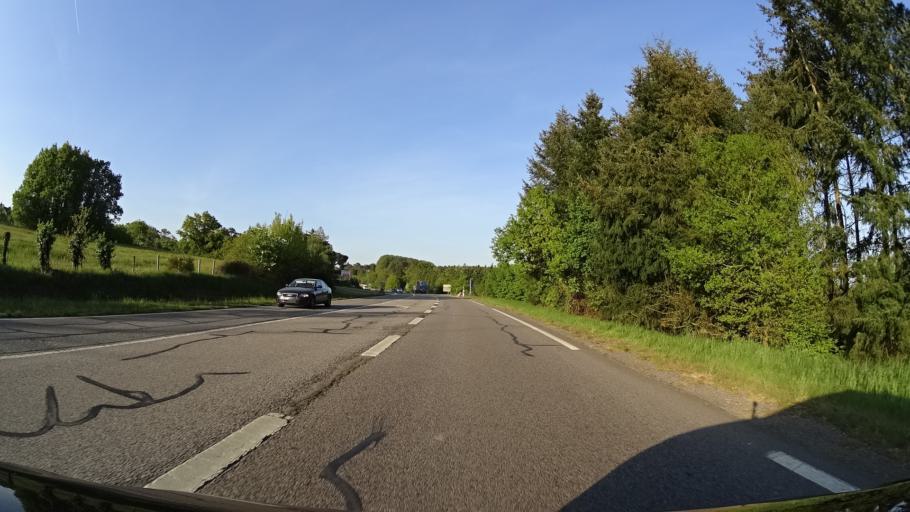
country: FR
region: Brittany
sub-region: Departement d'Ille-et-Vilaine
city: Sainte-Marie
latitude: 47.7180
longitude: -1.9743
